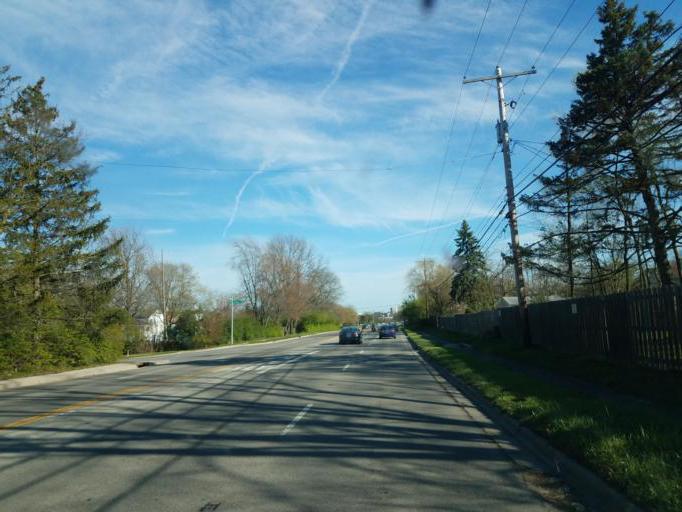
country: US
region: Ohio
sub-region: Franklin County
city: Upper Arlington
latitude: 40.0224
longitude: -83.0419
